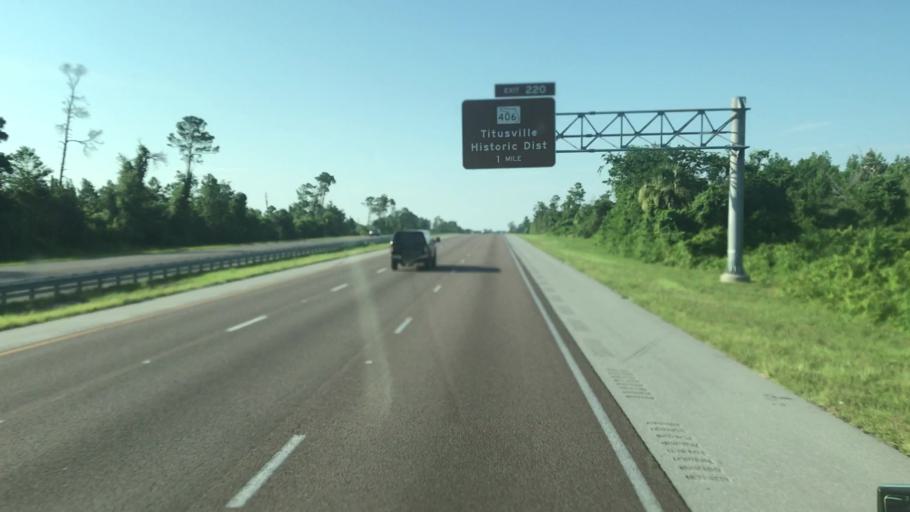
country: US
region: Florida
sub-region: Brevard County
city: Mims
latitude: 28.6353
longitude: -80.8572
